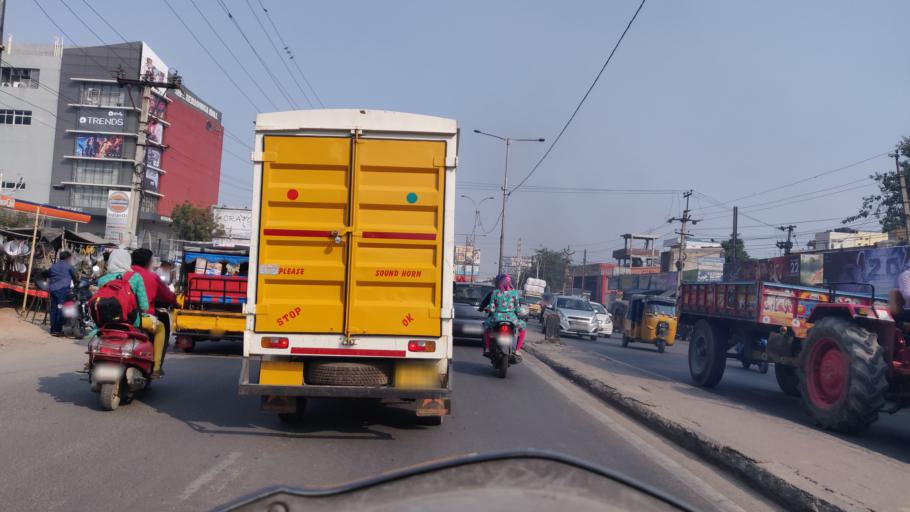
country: IN
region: Telangana
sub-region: Rangareddi
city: Uppal Kalan
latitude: 17.4015
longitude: 78.5710
